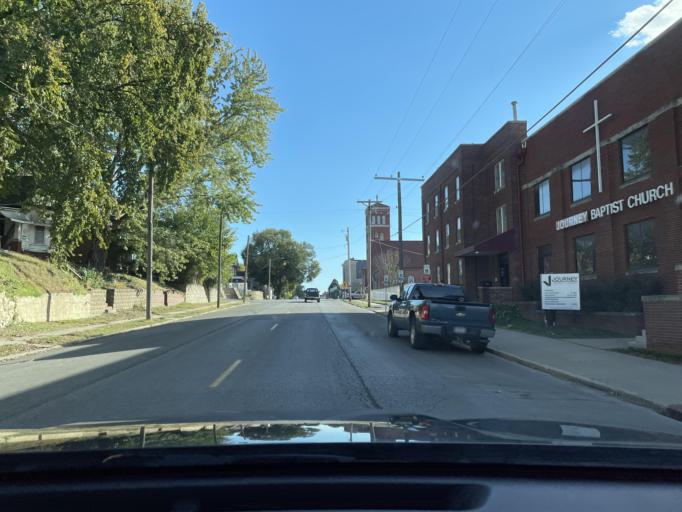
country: US
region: Kansas
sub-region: Doniphan County
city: Elwood
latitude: 39.7167
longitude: -94.8623
